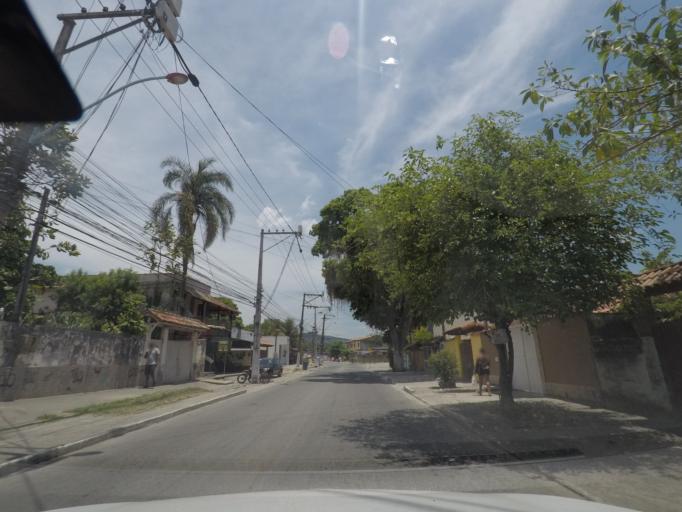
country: BR
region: Rio de Janeiro
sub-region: Marica
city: Marica
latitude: -22.9118
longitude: -42.8243
